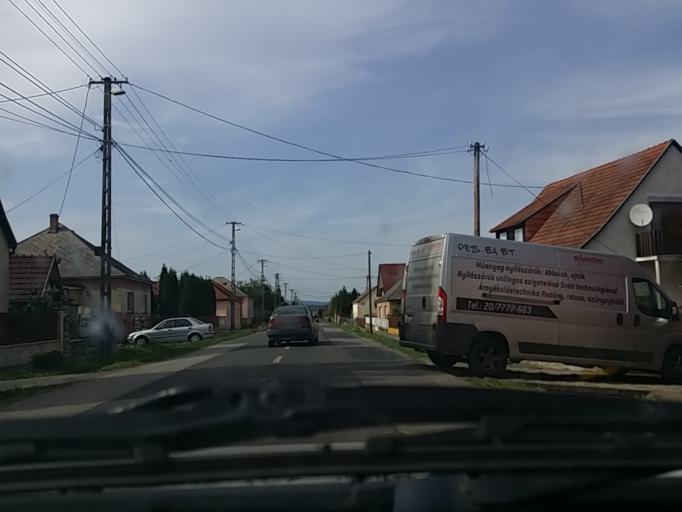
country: HU
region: Baranya
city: Harkany
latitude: 45.9436
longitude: 18.2378
